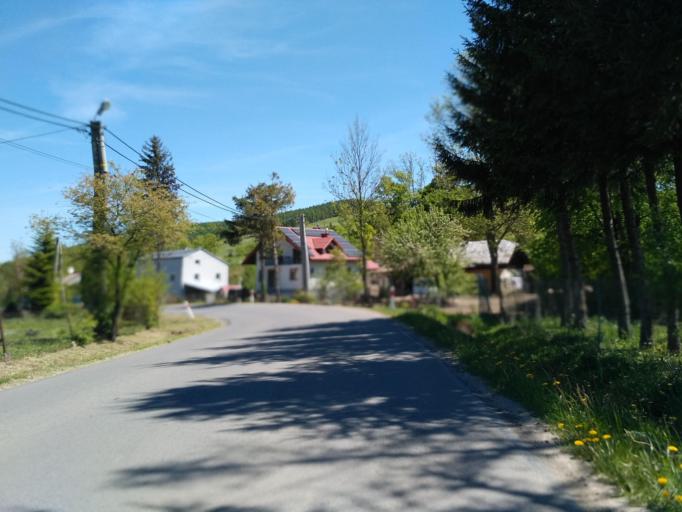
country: PL
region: Subcarpathian Voivodeship
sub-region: Powiat sanocki
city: Bukowsko
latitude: 49.5193
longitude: 22.0330
